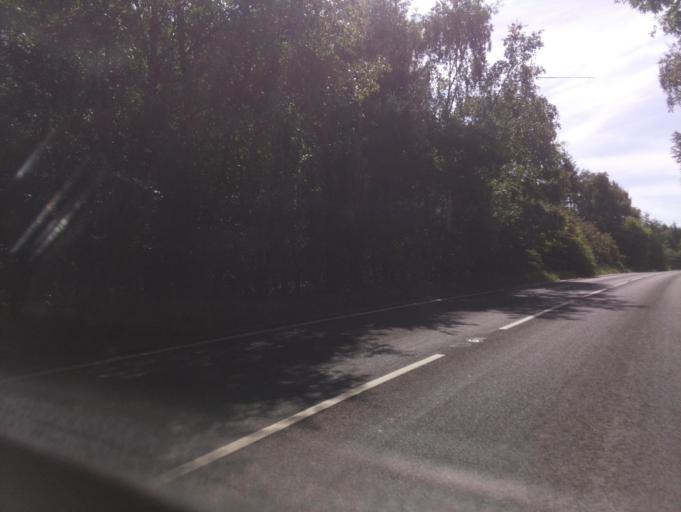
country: GB
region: England
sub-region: North Lincolnshire
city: Broughton
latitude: 53.5484
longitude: -0.5790
